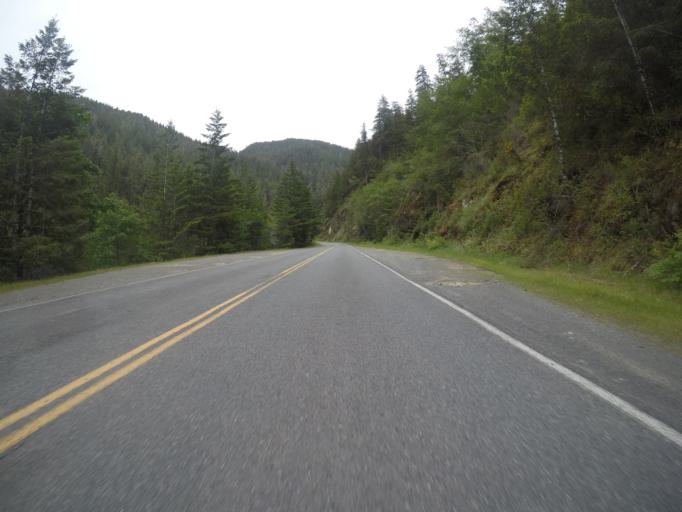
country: US
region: California
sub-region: Del Norte County
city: Bertsch-Oceanview
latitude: 41.7802
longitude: -124.0186
